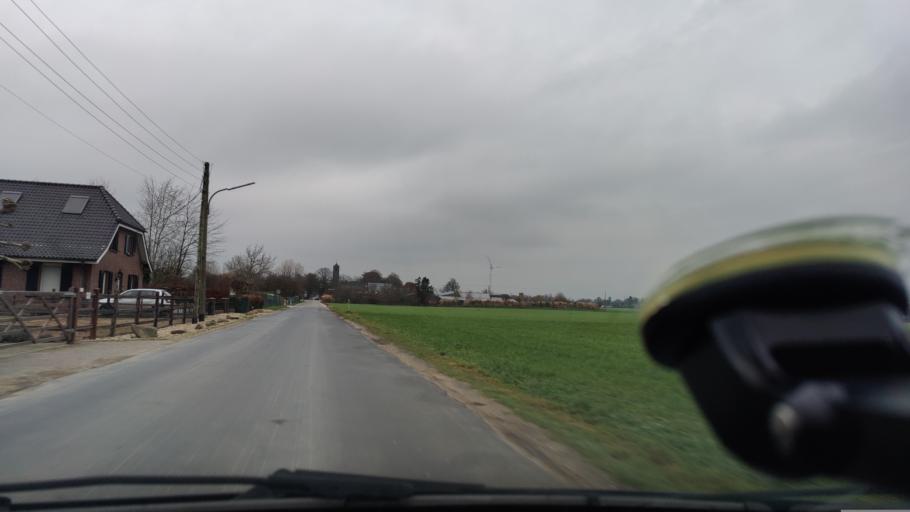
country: DE
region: North Rhine-Westphalia
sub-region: Regierungsbezirk Dusseldorf
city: Goch
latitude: 51.7144
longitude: 6.1857
